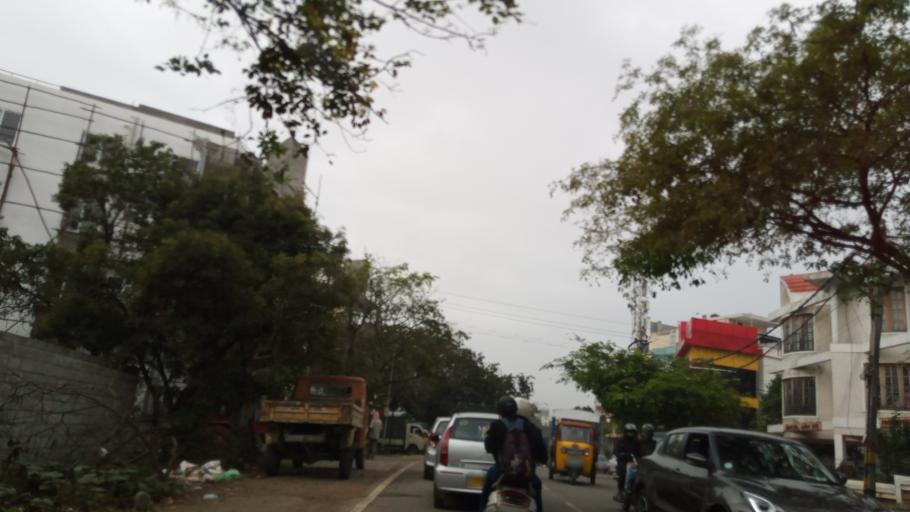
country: IN
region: Karnataka
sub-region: Bangalore Urban
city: Bangalore
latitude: 12.9088
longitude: 77.5351
